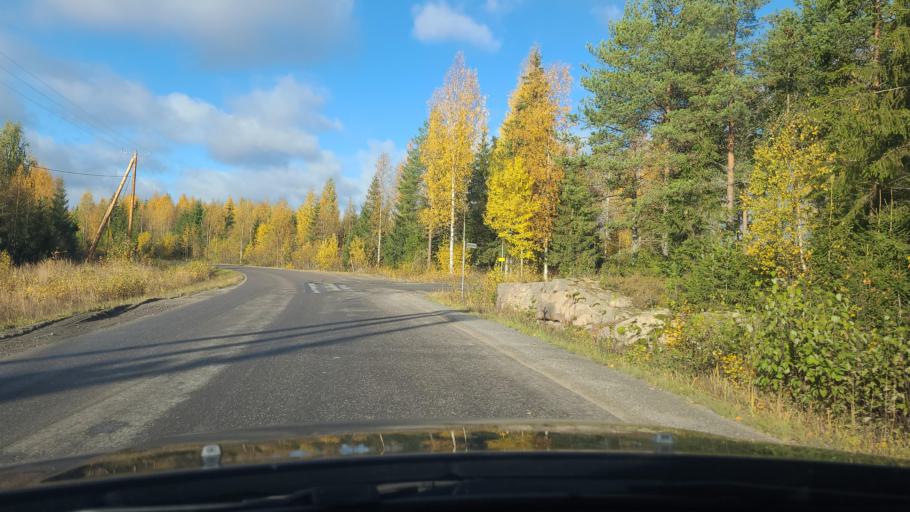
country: FI
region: Southern Savonia
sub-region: Pieksaemaeki
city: Juva
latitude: 61.8823
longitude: 27.7539
